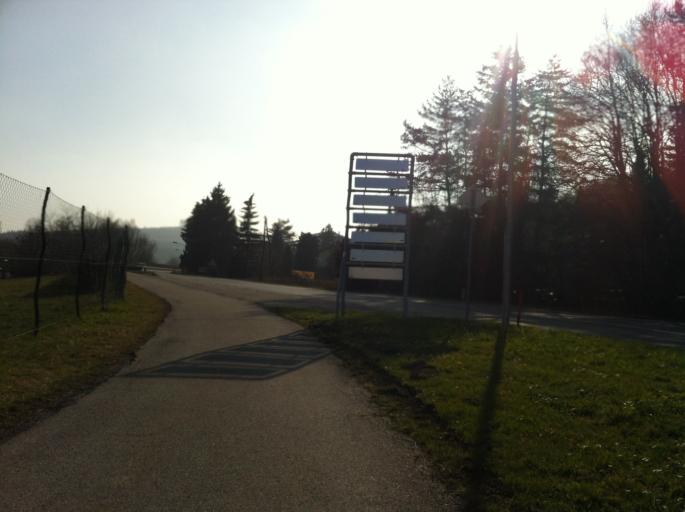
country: AT
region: Lower Austria
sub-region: Politischer Bezirk Wien-Umgebung
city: Wolfsgraben
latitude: 48.1857
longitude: 16.1230
